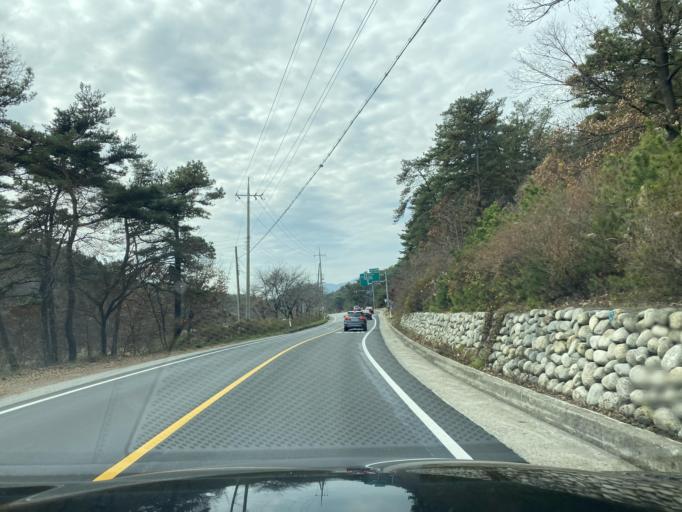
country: KR
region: Chungcheongnam-do
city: Hongsung
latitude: 36.6578
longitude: 126.6265
